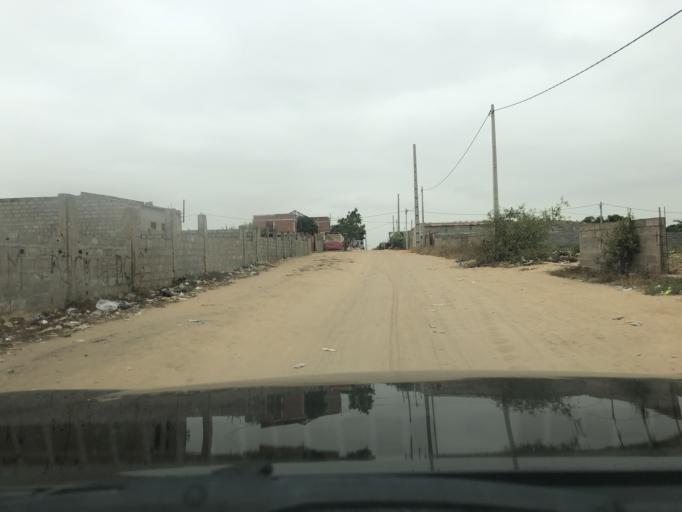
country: AO
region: Luanda
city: Luanda
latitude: -8.9383
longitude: 13.2303
